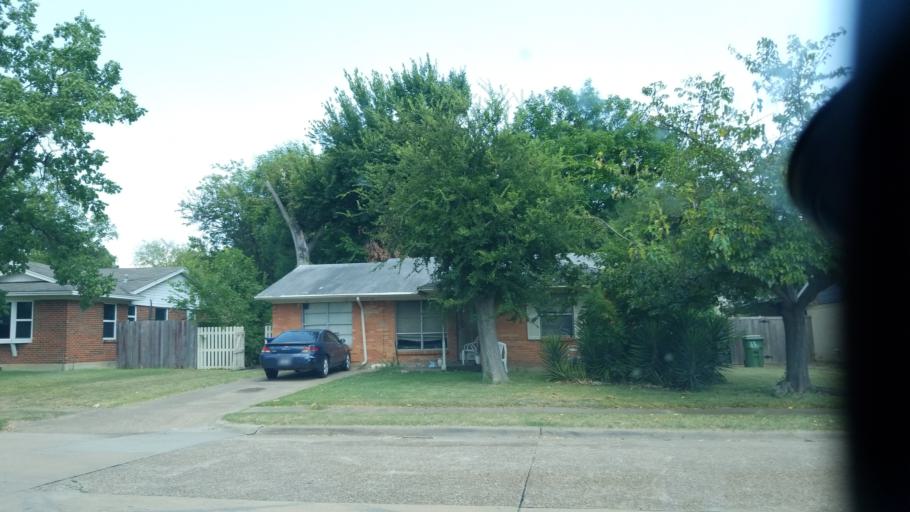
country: US
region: Texas
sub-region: Dallas County
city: Garland
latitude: 32.9250
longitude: -96.6445
